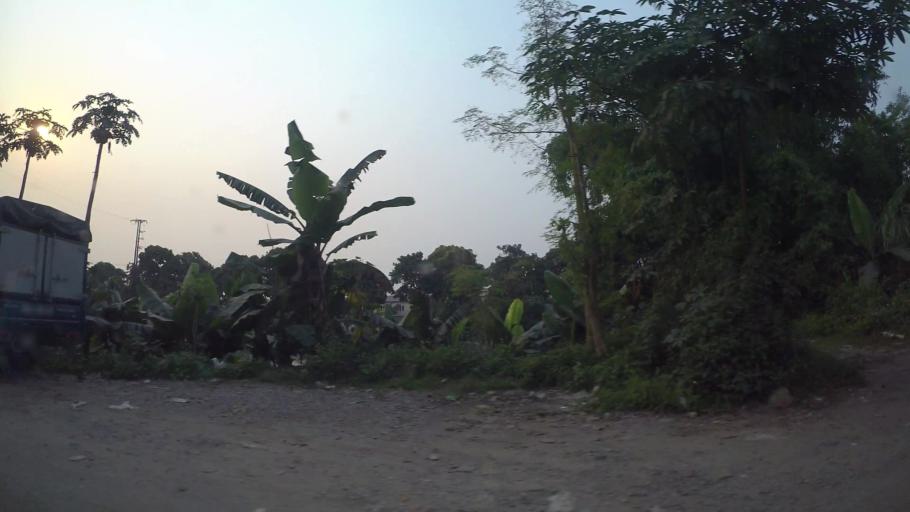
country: VN
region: Ha Noi
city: Kim Bai
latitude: 20.8686
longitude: 105.8127
